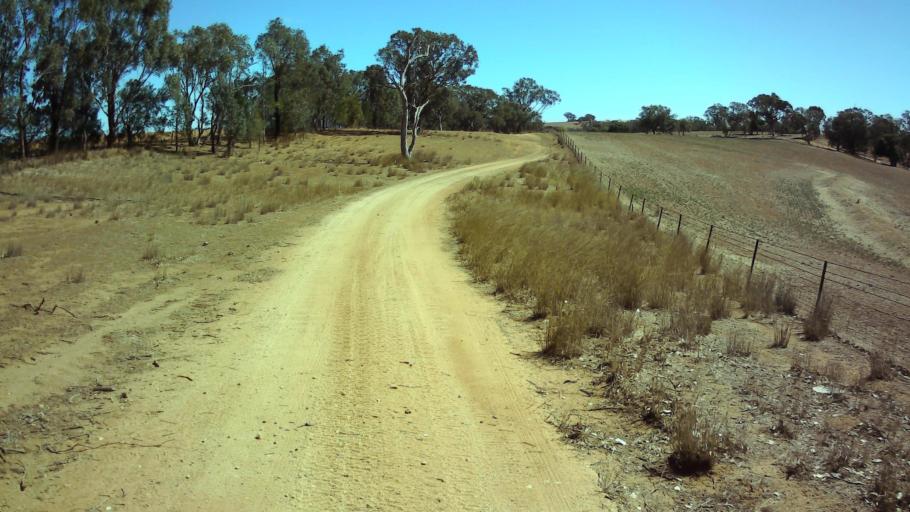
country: AU
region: New South Wales
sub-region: Weddin
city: Grenfell
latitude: -33.9943
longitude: 148.4366
